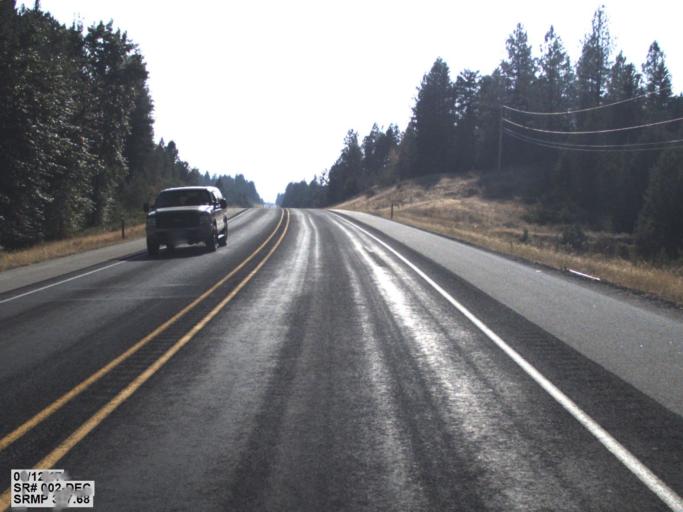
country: US
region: Washington
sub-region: Pend Oreille County
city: Newport
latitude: 48.1394
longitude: -117.1612
